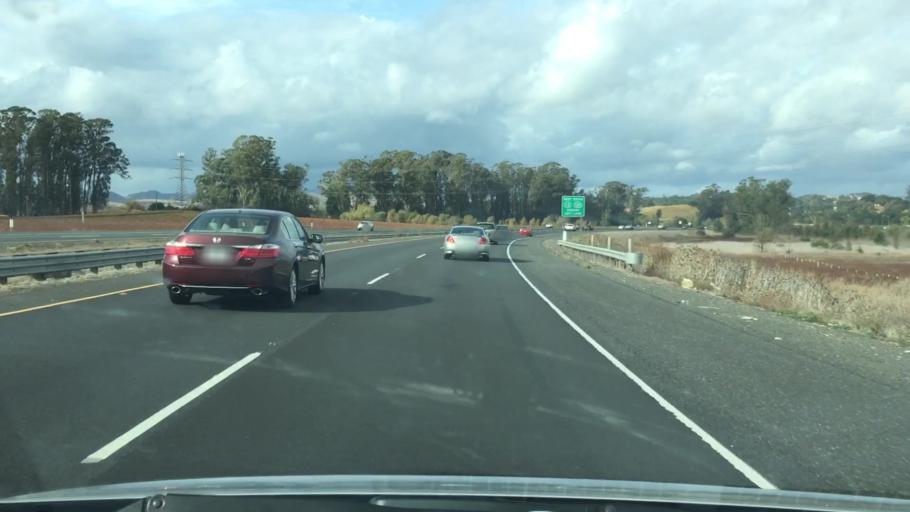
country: US
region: California
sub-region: Napa County
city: Napa
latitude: 38.2500
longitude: -122.3012
